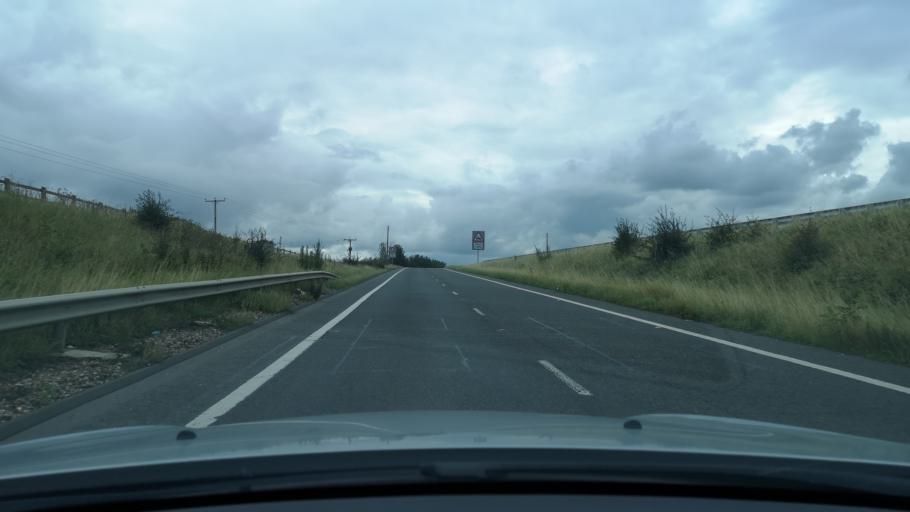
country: GB
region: England
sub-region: City and Borough of Wakefield
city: Darrington
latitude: 53.6930
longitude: -1.2665
